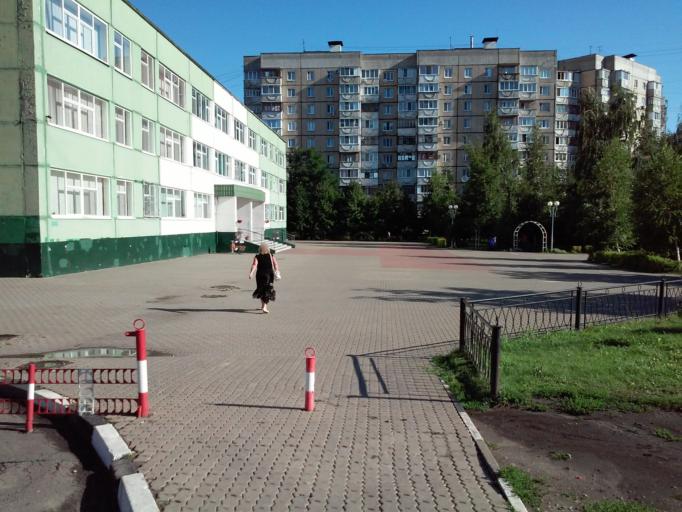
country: RU
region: Belgorod
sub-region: Belgorodskiy Rayon
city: Belgorod
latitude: 50.5580
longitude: 36.5686
